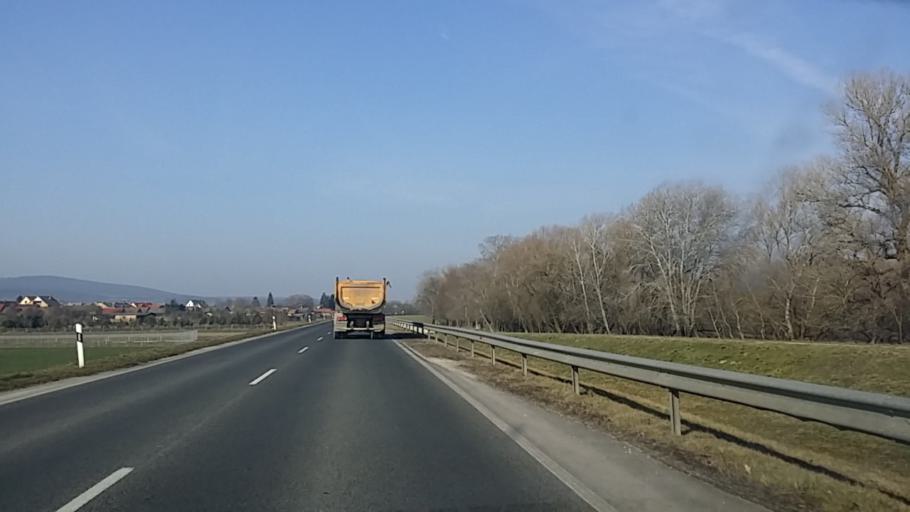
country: HU
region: Komarom-Esztergom
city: Tat
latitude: 47.7484
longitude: 18.6447
